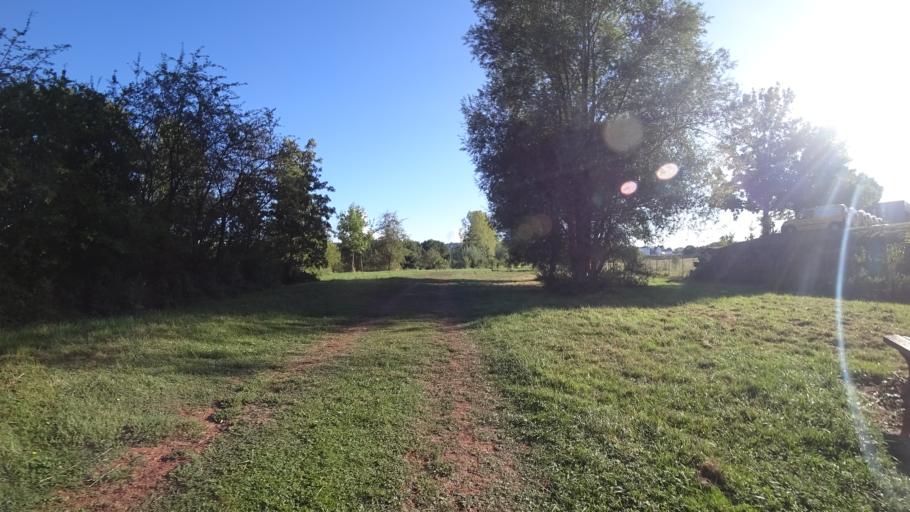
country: FR
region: Midi-Pyrenees
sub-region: Departement de l'Aveyron
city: Rodez
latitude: 44.3717
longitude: 2.5816
